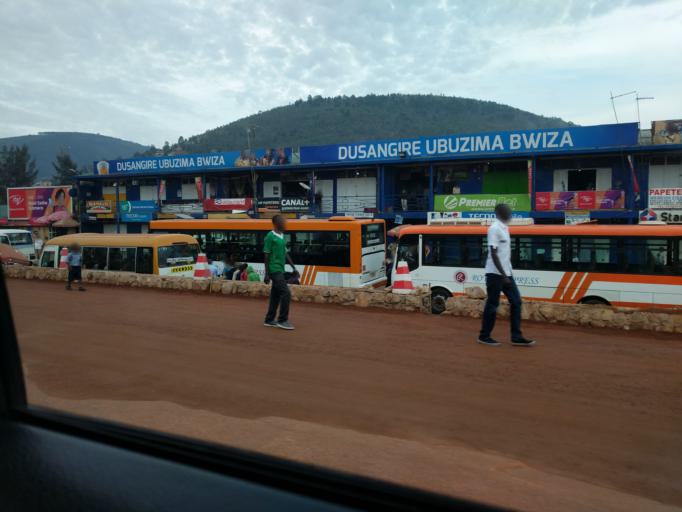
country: RW
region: Kigali
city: Kigali
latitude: -1.9415
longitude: 30.0451
